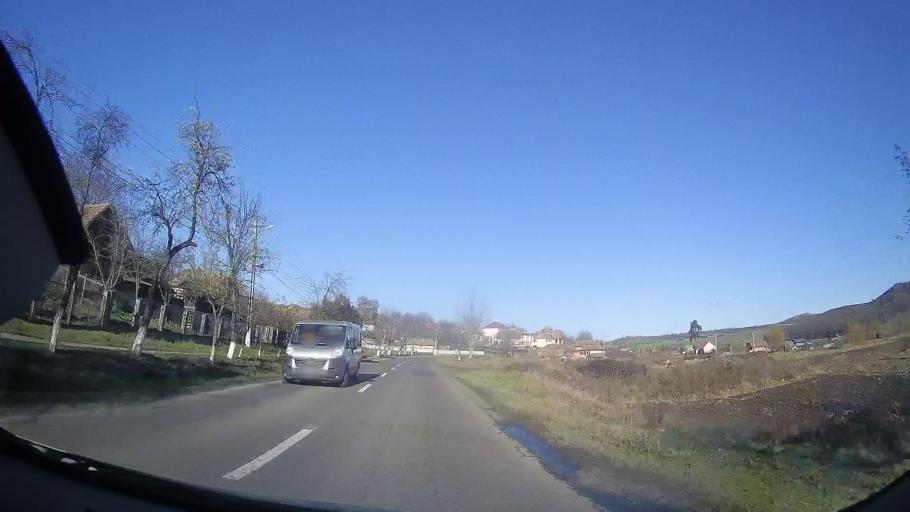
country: RO
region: Mures
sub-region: Comuna Sarmasu
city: Balda
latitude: 46.7285
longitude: 24.1444
